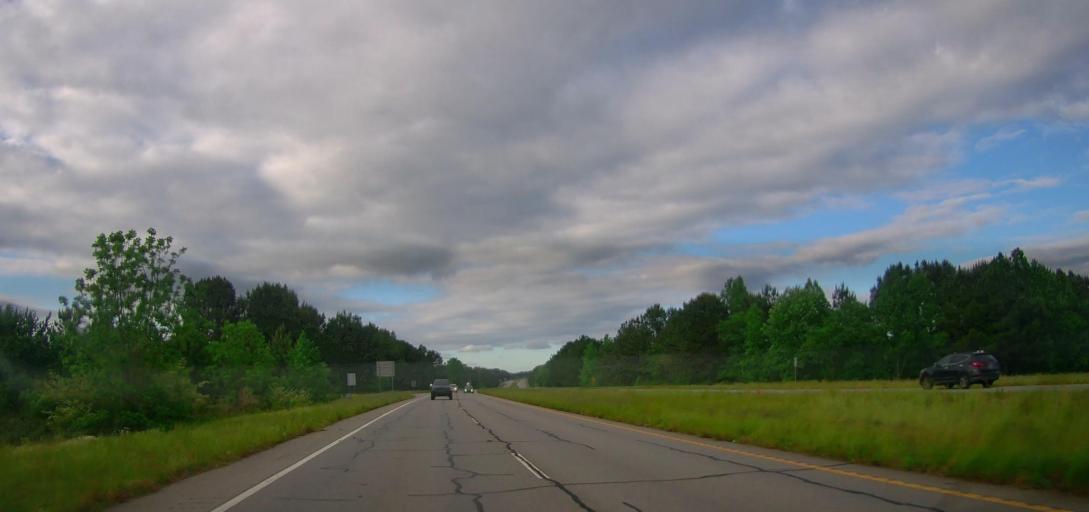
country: US
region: Georgia
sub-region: Oconee County
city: Watkinsville
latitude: 33.8677
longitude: -83.4236
